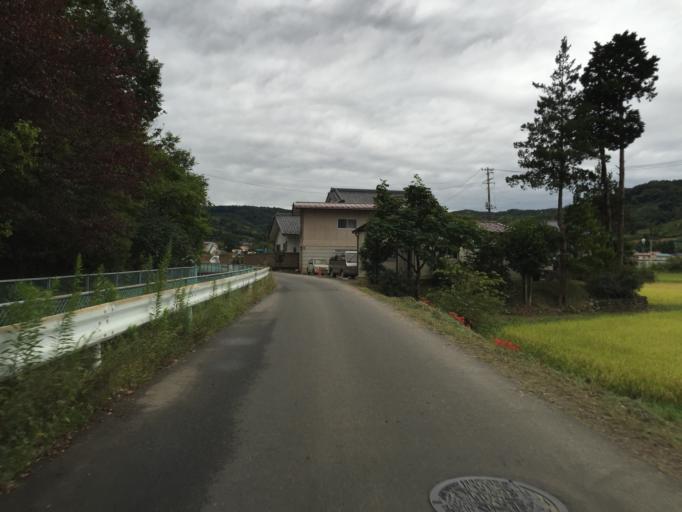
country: JP
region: Fukushima
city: Fukushima-shi
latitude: 37.7704
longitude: 140.5134
